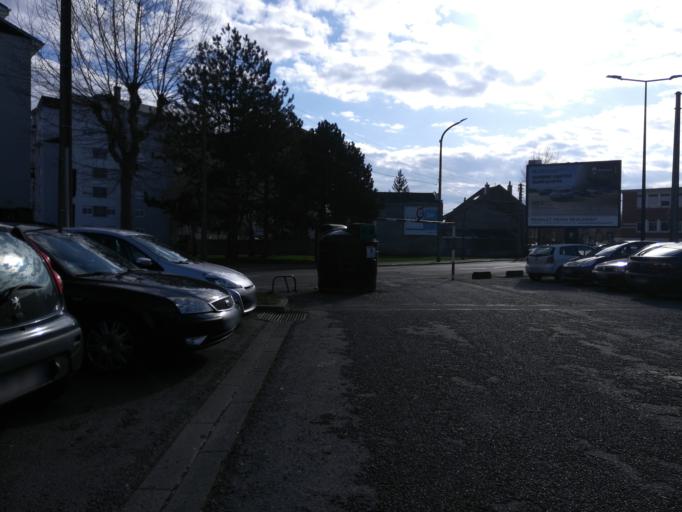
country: FR
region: Nord-Pas-de-Calais
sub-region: Departement du Pas-de-Calais
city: Montigny-en-Gohelle
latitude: 50.4308
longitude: 2.9491
